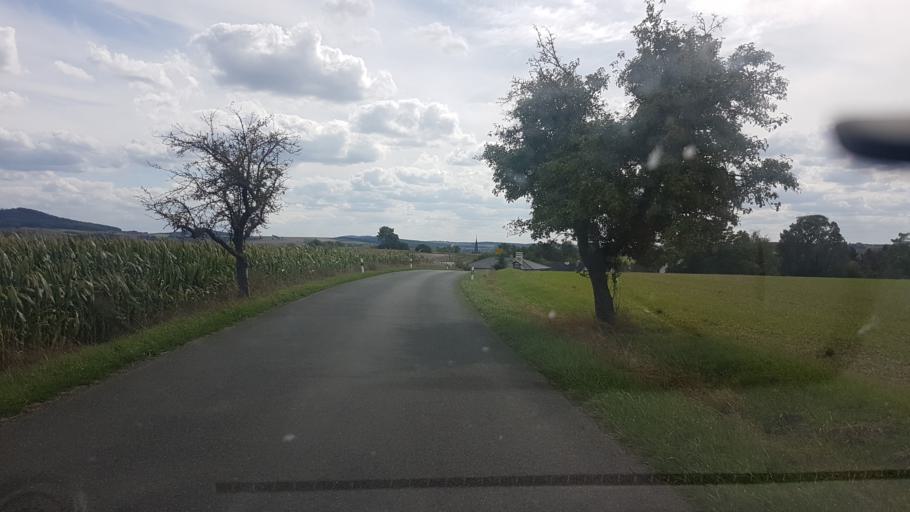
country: DE
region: Bavaria
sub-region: Upper Franconia
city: Untersiemau
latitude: 50.2049
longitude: 10.9557
